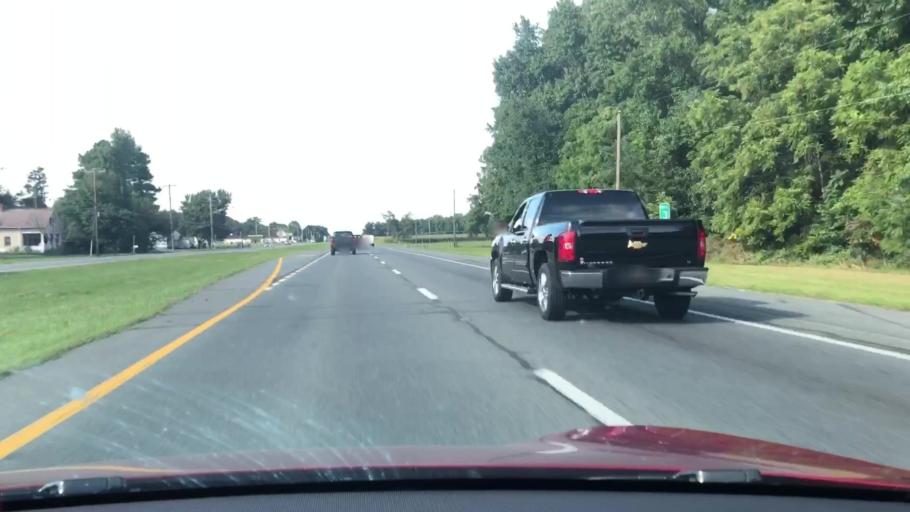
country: US
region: Delaware
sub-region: Kent County
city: Felton
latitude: 39.0106
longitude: -75.5679
